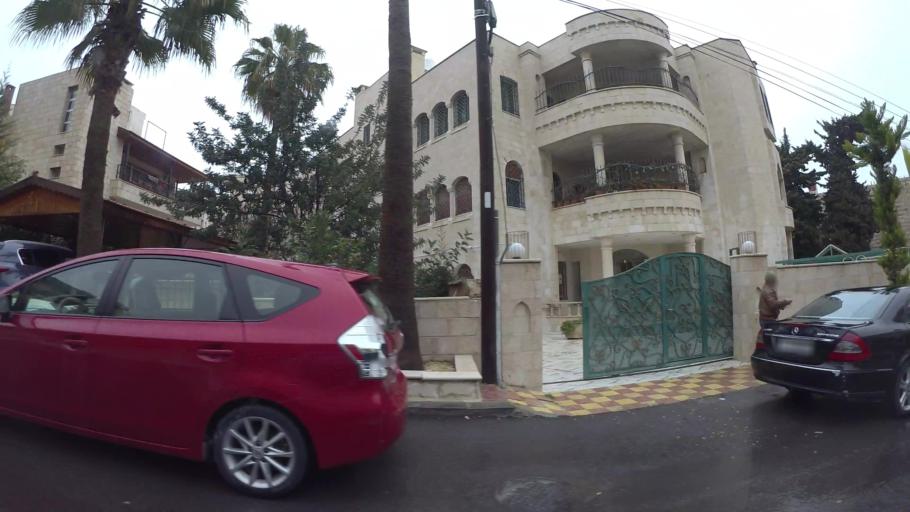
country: JO
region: Amman
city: Wadi as Sir
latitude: 31.9617
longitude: 35.8547
